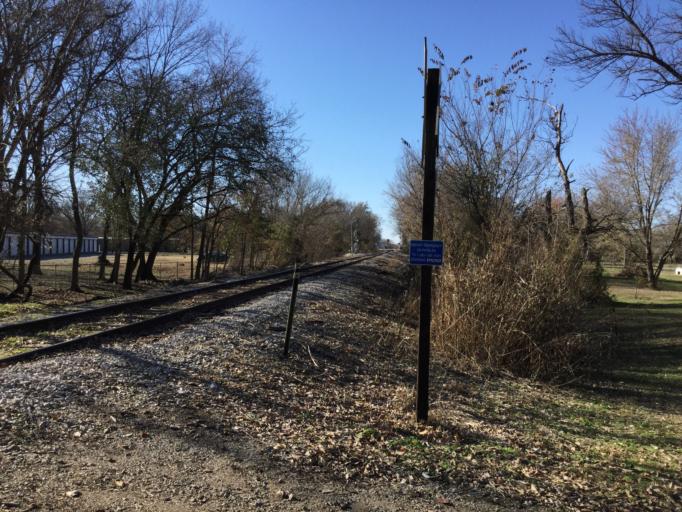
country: US
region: Kansas
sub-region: Montgomery County
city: Cherryvale
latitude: 37.2719
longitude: -95.5449
